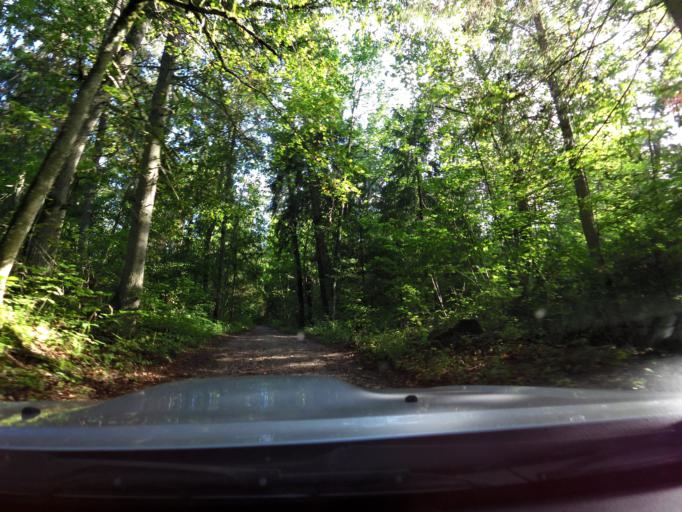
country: LT
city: Trakai
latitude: 54.6459
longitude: 24.9763
